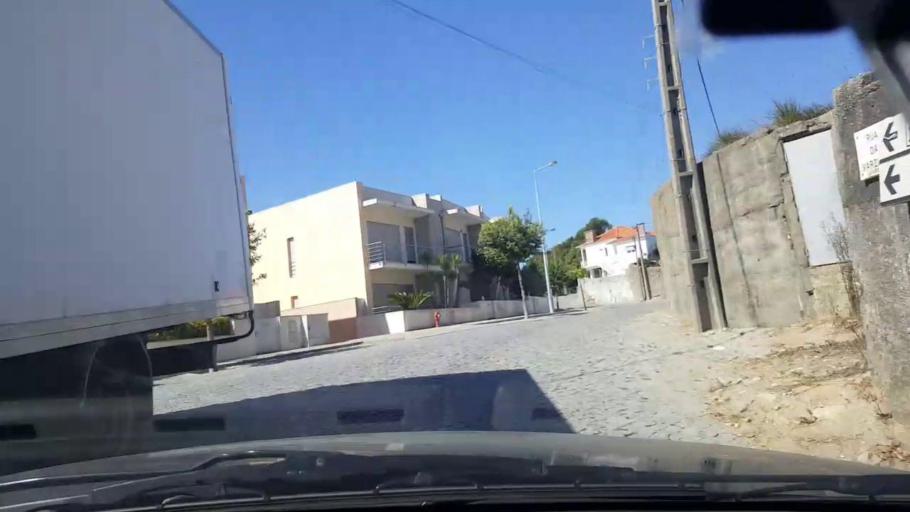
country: PT
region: Porto
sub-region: Vila do Conde
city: Arvore
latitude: 41.3368
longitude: -8.7169
